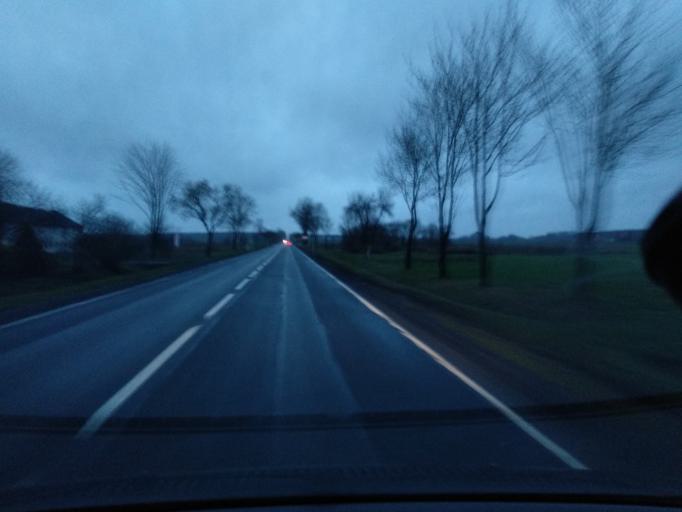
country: PL
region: Lower Silesian Voivodeship
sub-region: Powiat legnicki
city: Prochowice
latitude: 51.2328
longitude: 16.4223
